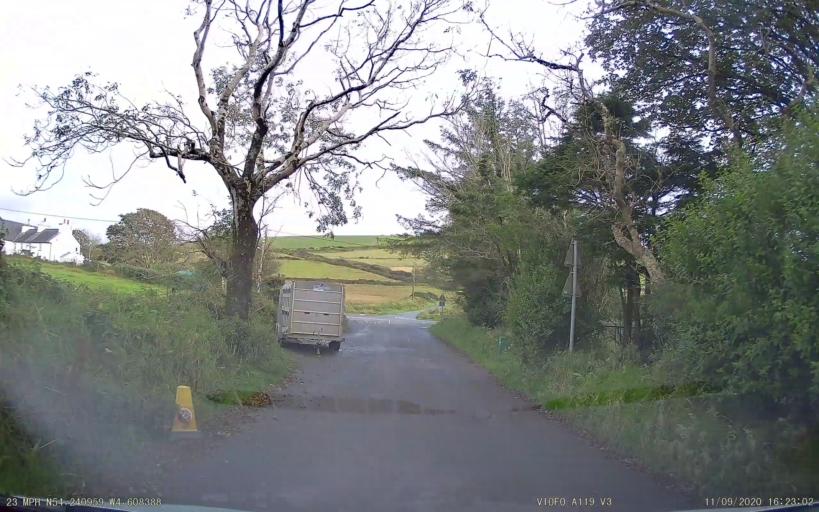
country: IM
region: Douglas
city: Douglas
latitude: 54.2410
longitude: -4.6084
